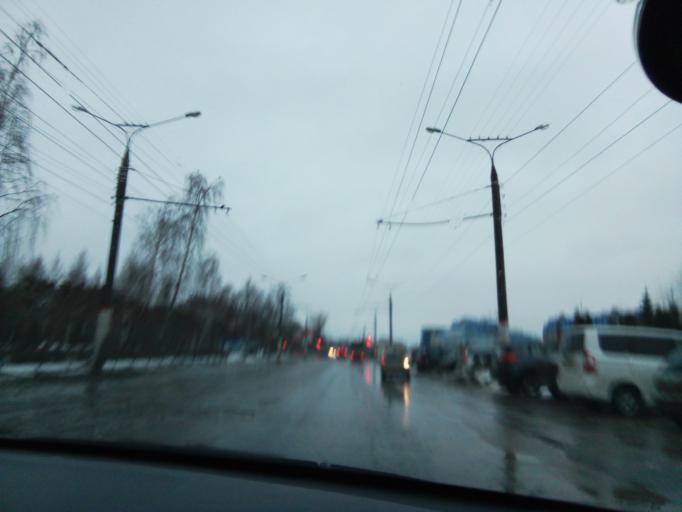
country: RU
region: Chuvashia
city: Novyye Lapsary
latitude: 56.1186
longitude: 47.1950
